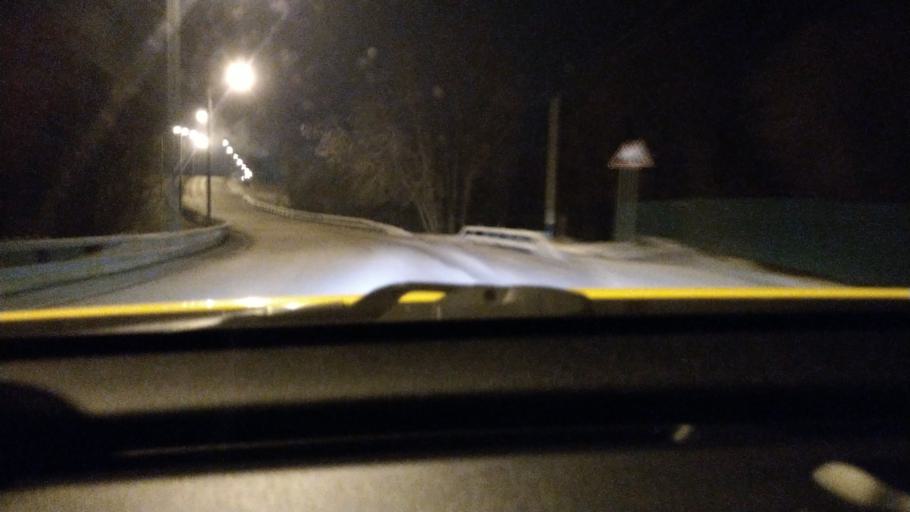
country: RU
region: Moskovskaya
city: Troitsk
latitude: 55.4431
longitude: 37.2697
